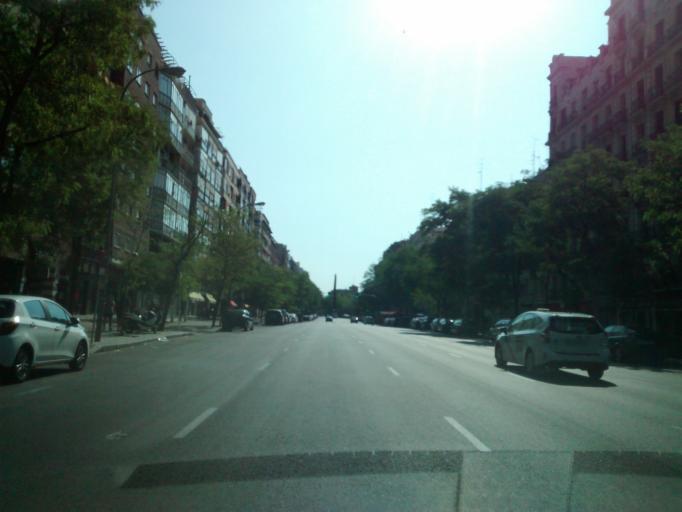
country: ES
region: Madrid
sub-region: Provincia de Madrid
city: Arganzuela
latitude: 40.4010
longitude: -3.6978
